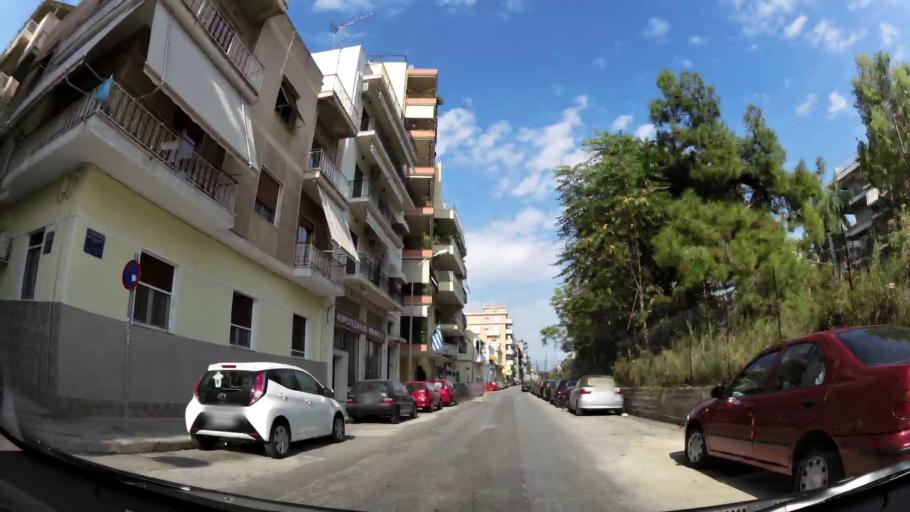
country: GR
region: Attica
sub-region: Nomarchia Athinas
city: Kipseli
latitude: 37.9982
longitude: 23.7201
